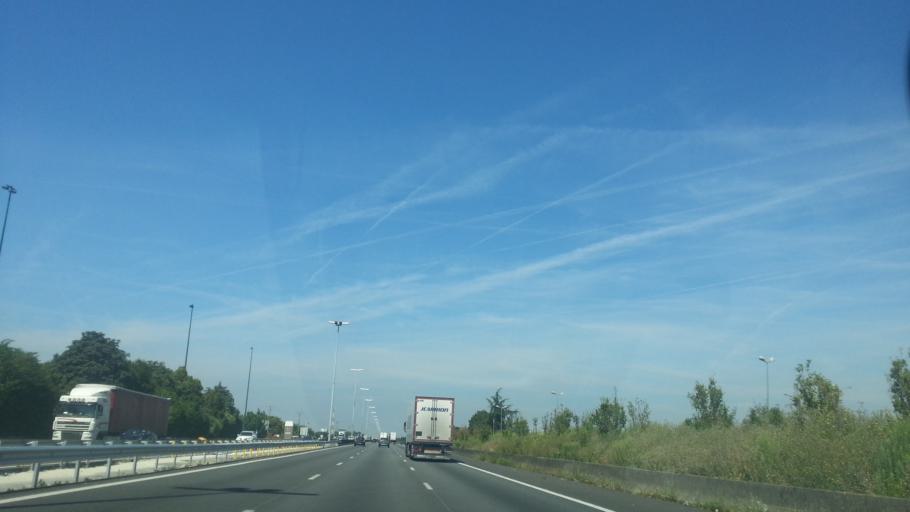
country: FR
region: Ile-de-France
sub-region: Departement du Val-d'Oise
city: Vemars
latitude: 49.0725
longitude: 2.5523
